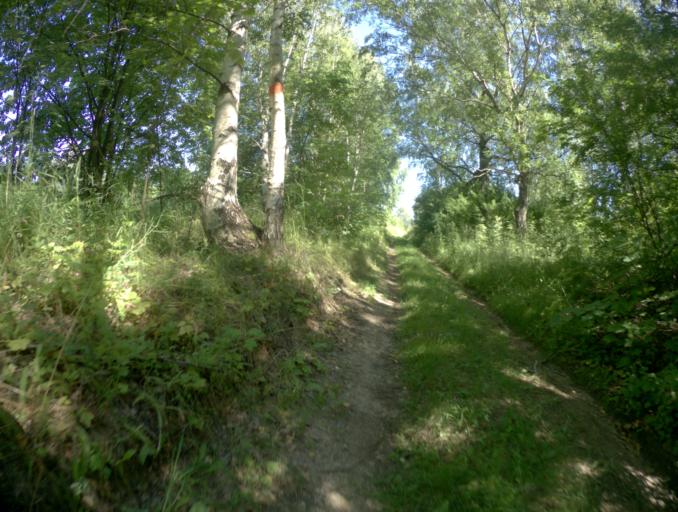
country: RU
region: Nizjnij Novgorod
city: Gorbatov
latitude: 56.0773
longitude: 43.0997
